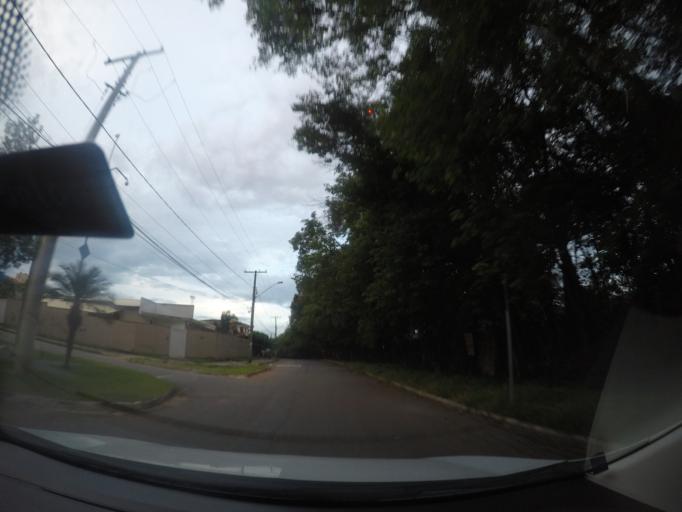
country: BR
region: Goias
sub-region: Goiania
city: Goiania
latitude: -16.6476
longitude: -49.2234
